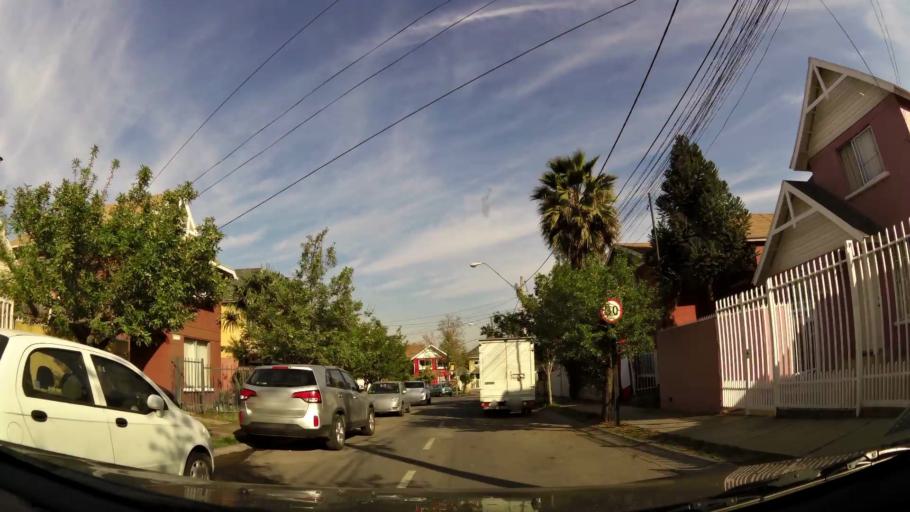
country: CL
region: Santiago Metropolitan
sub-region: Provincia de Cordillera
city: Puente Alto
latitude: -33.5580
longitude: -70.5468
